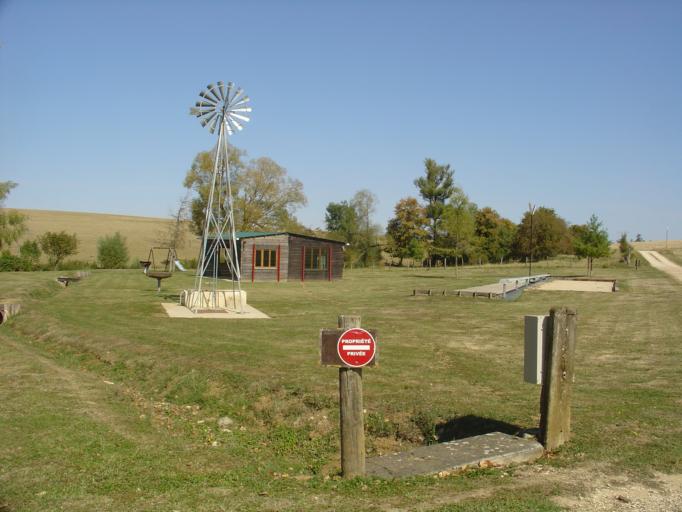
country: FR
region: Lorraine
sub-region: Departement de Meurthe-et-Moselle
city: Colombey-les-Belles
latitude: 48.5551
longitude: 5.8687
